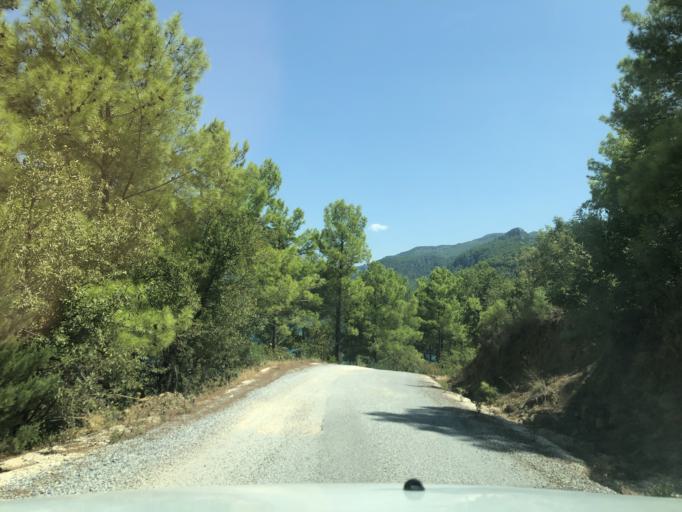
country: TR
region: Antalya
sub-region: Manavgat
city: Manavgat
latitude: 36.9109
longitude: 31.5498
